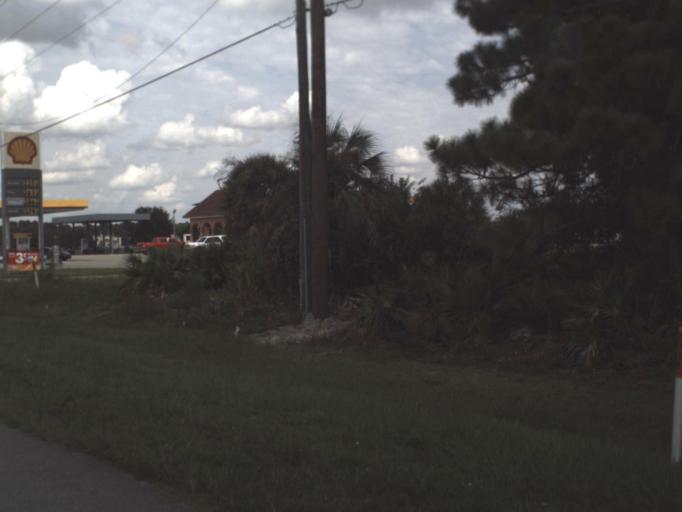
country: US
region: Florida
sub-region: Hendry County
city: LaBelle
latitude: 26.7339
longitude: -81.4377
